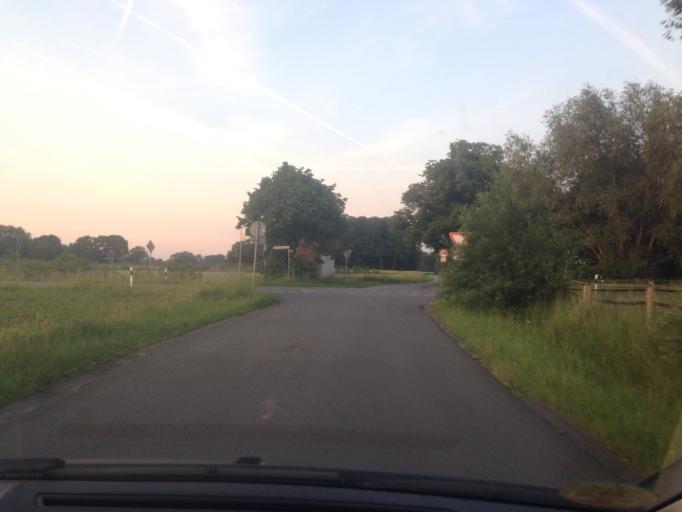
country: DE
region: North Rhine-Westphalia
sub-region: Regierungsbezirk Munster
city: Greven
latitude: 52.0364
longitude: 7.5941
